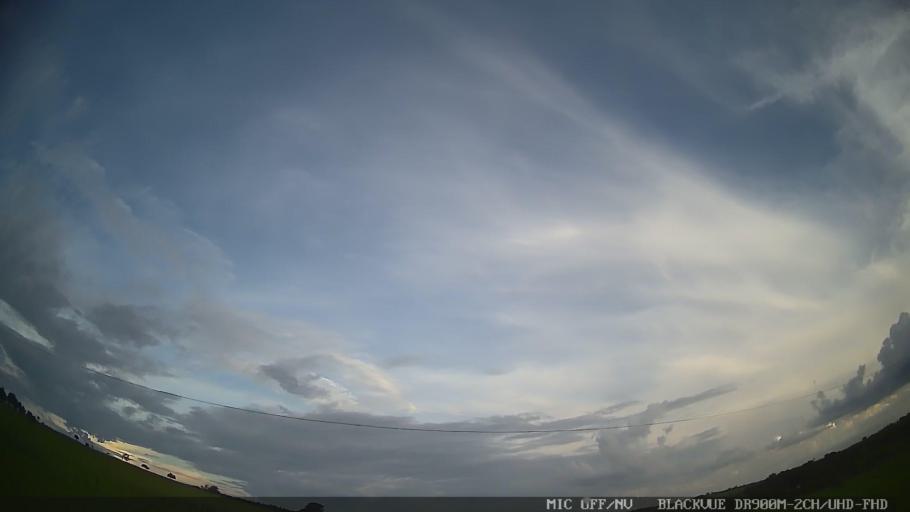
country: BR
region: Sao Paulo
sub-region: Jaguariuna
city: Jaguariuna
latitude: -22.7299
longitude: -47.0145
